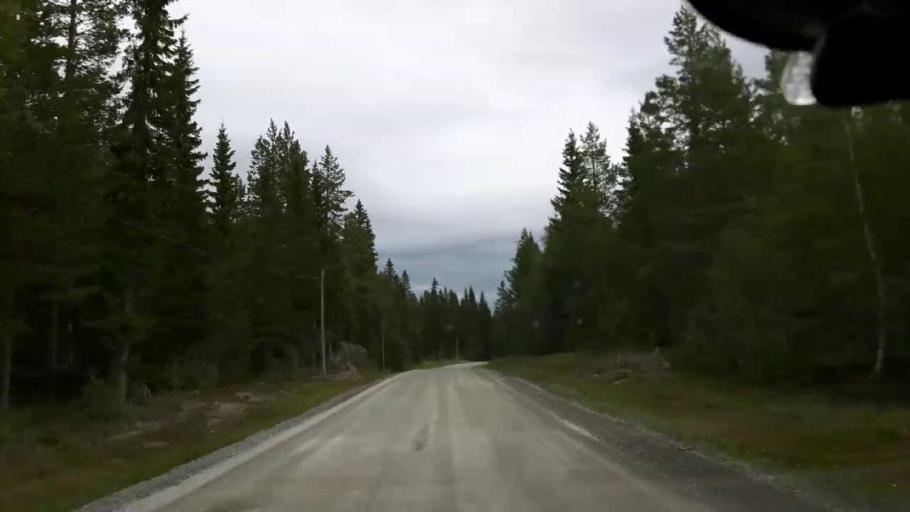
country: SE
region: Jaemtland
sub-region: OEstersunds Kommun
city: Brunflo
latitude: 63.1044
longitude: 14.9846
